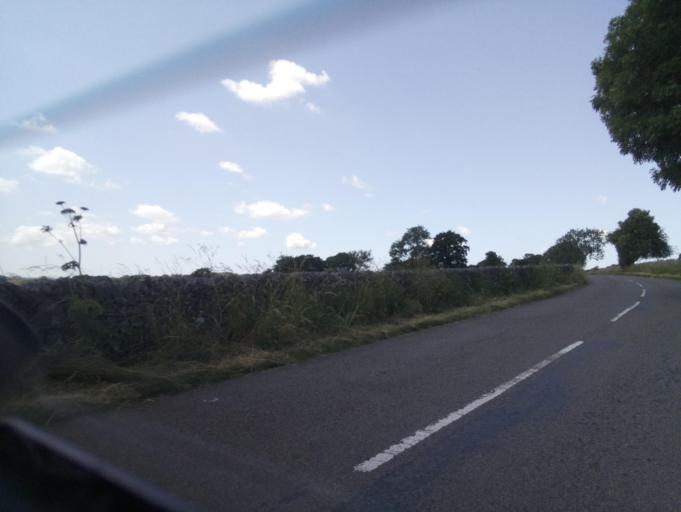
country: GB
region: England
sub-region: Derbyshire
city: Tideswell
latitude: 53.2601
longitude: -1.8047
